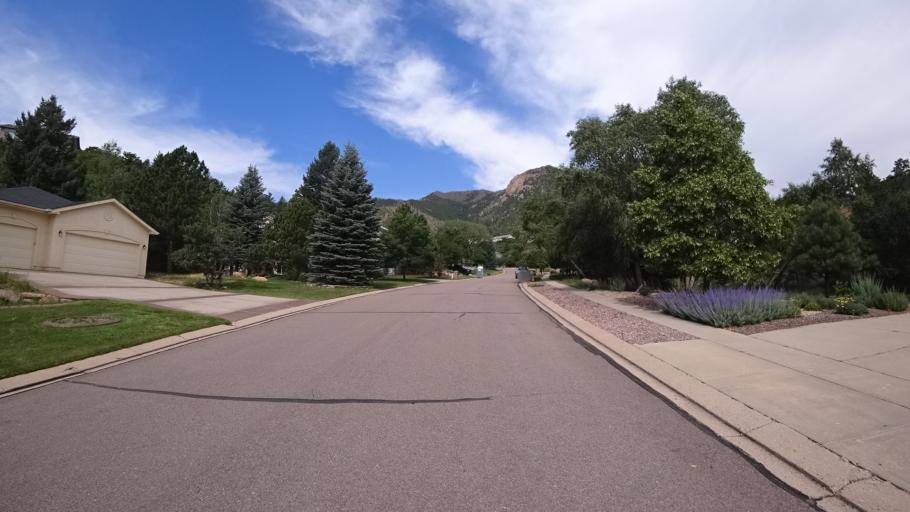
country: US
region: Colorado
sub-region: El Paso County
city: Air Force Academy
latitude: 38.9520
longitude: -104.8855
